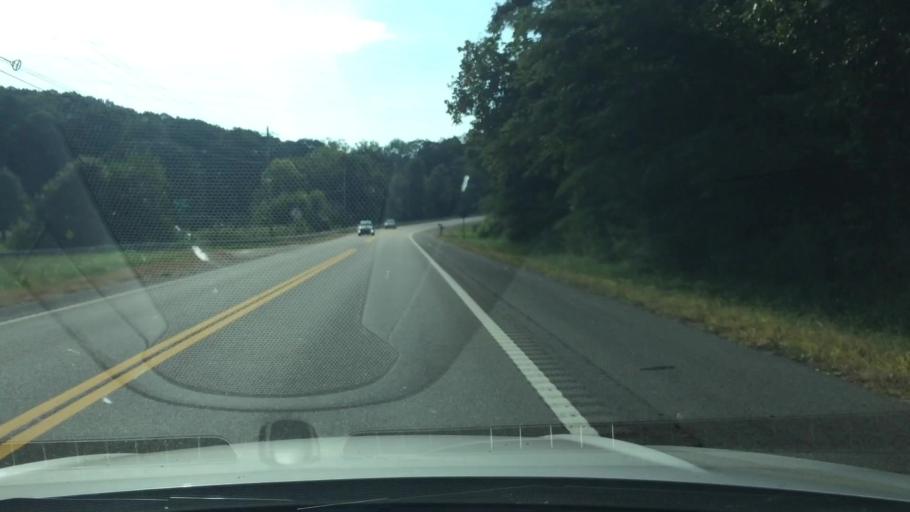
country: US
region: Tennessee
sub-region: McMinn County
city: Athens
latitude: 35.4969
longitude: -84.6041
